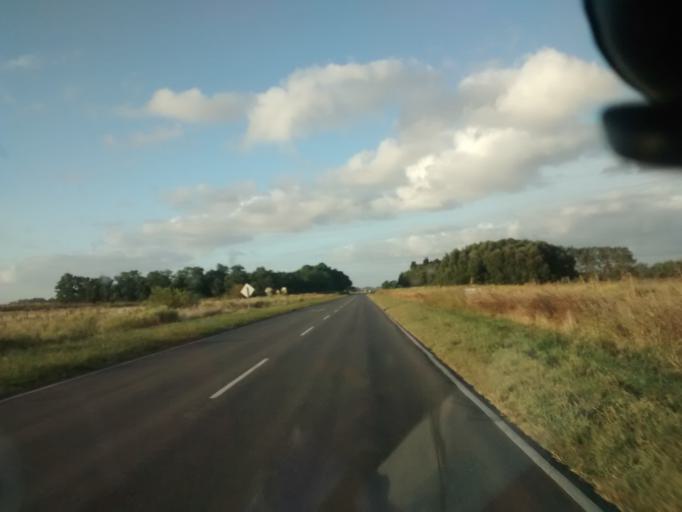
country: AR
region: Buenos Aires
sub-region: Partido de General Belgrano
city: General Belgrano
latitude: -35.8032
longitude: -58.5573
